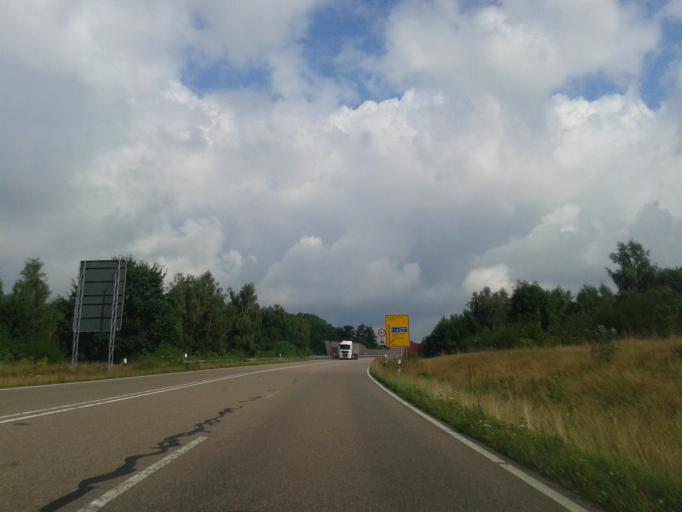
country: DE
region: Saxony
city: Radeberg
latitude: 51.1174
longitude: 13.9329
